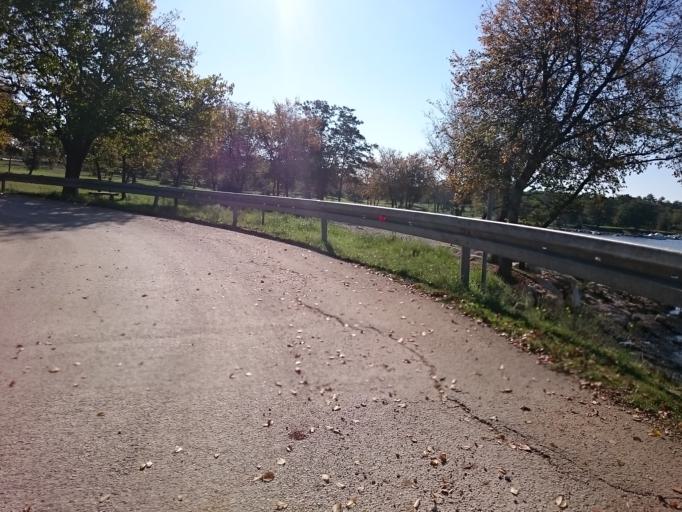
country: HR
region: Istarska
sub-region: Grad Porec
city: Porec
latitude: 45.2529
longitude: 13.5958
